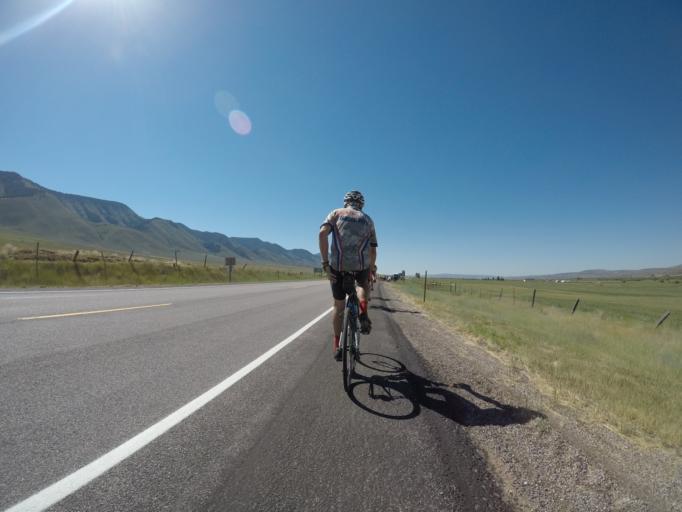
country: US
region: Idaho
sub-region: Bear Lake County
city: Montpelier
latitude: 42.3509
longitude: -111.0474
